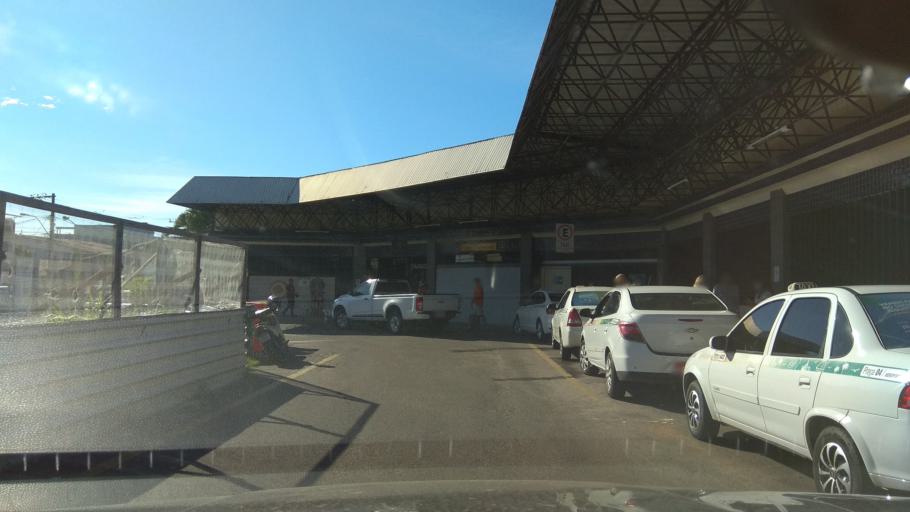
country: BR
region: Bahia
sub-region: Ilheus
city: Ilheus
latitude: -14.8140
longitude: -39.0318
